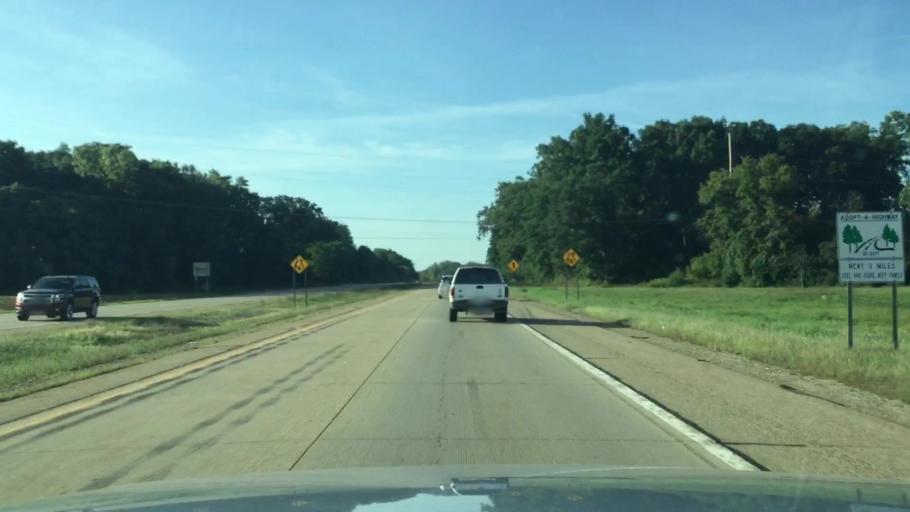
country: US
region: Michigan
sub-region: Jackson County
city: Vandercook Lake
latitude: 42.1957
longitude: -84.3698
